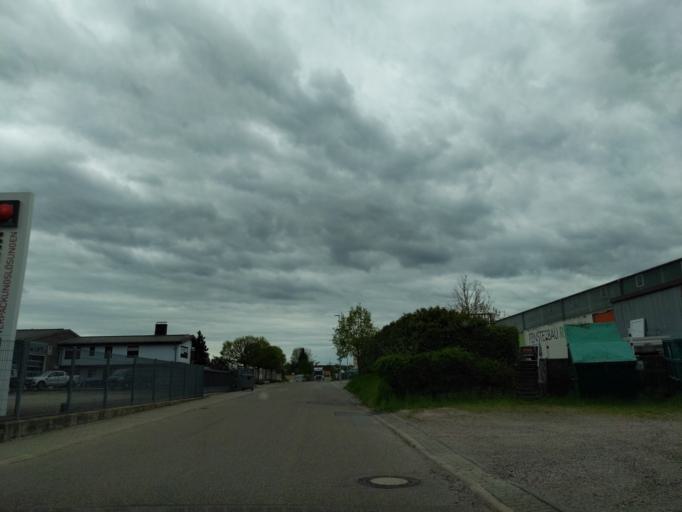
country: DE
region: Baden-Wuerttemberg
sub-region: Karlsruhe Region
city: Meckesheim
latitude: 49.3242
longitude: 8.8057
